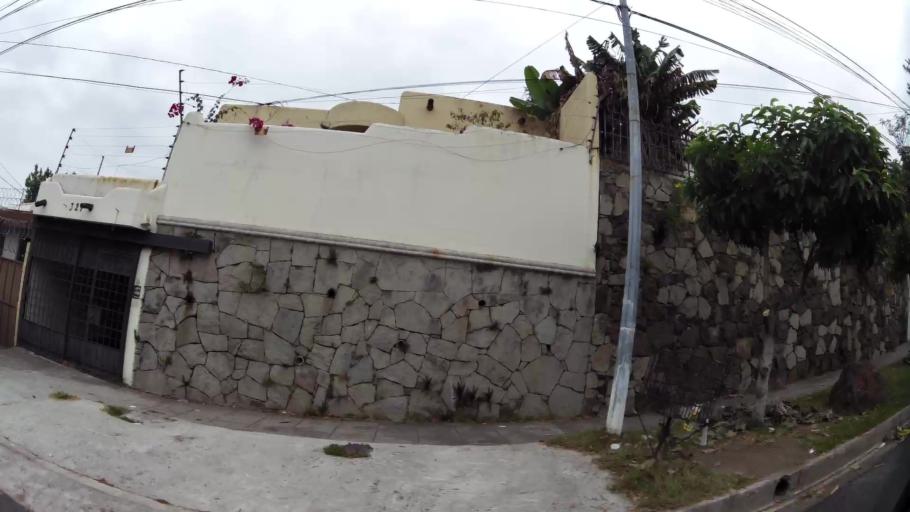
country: SV
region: La Libertad
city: Antiguo Cuscatlan
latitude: 13.7057
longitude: -89.2409
